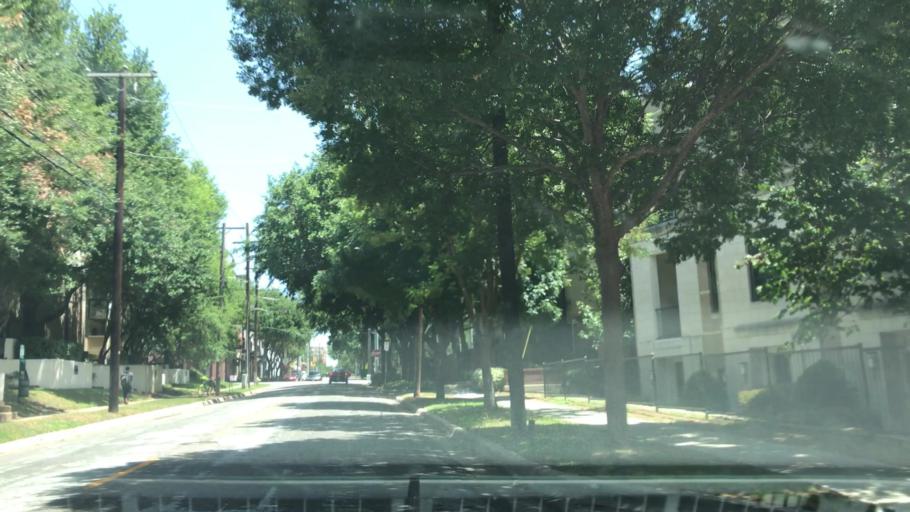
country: US
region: Texas
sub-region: Dallas County
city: Dallas
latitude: 32.8058
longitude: -96.8011
